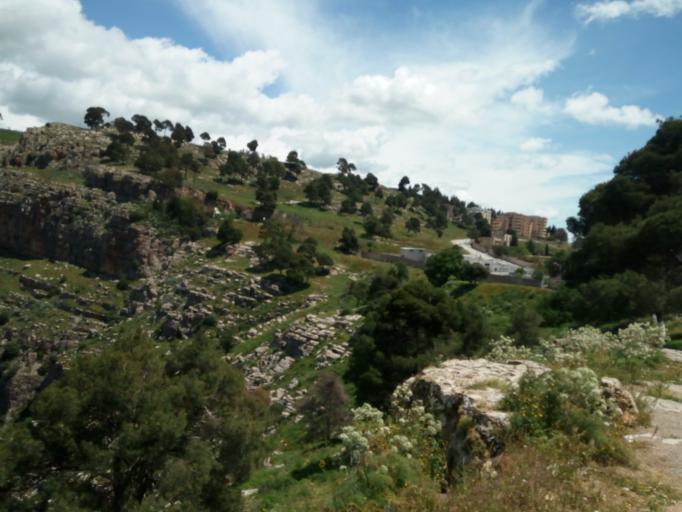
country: DZ
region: Constantine
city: Constantine
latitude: 36.3753
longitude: 6.6142
